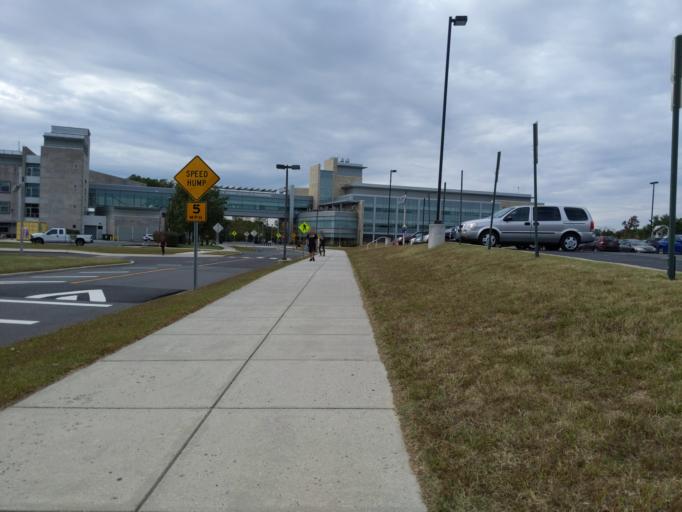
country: US
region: New Jersey
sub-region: Gloucester County
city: Glassboro
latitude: 39.7119
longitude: -75.1206
